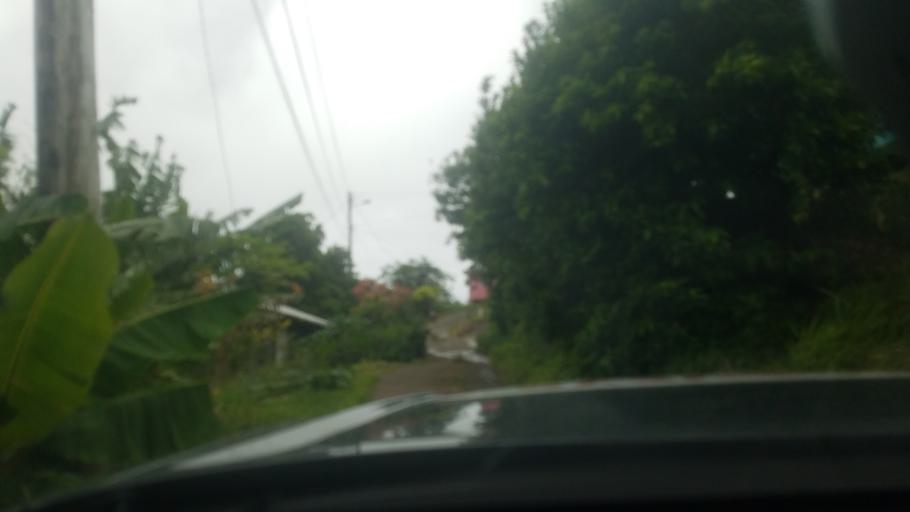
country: LC
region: Gros-Islet
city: Gros Islet
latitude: 14.0441
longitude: -60.9214
